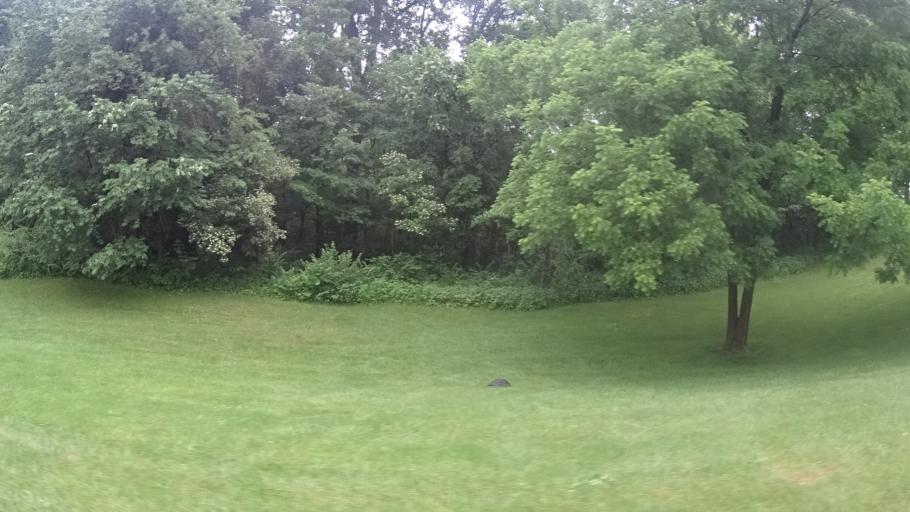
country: US
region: Ohio
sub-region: Erie County
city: Huron
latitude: 41.3577
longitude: -82.5646
